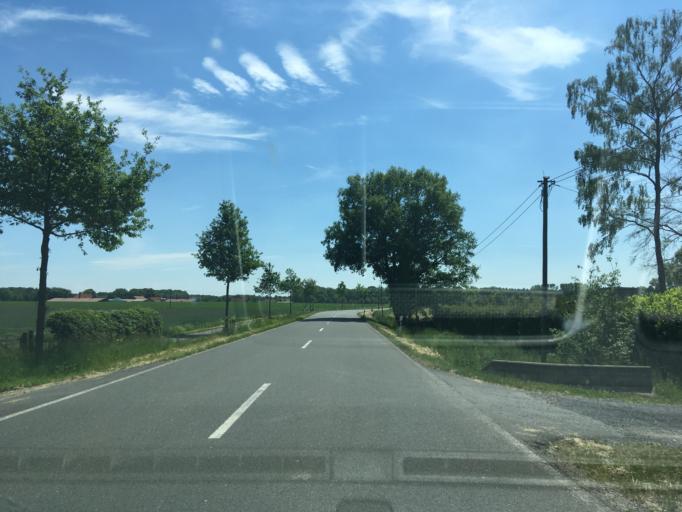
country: DE
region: North Rhine-Westphalia
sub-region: Regierungsbezirk Munster
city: Borken
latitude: 51.8709
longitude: 6.8312
